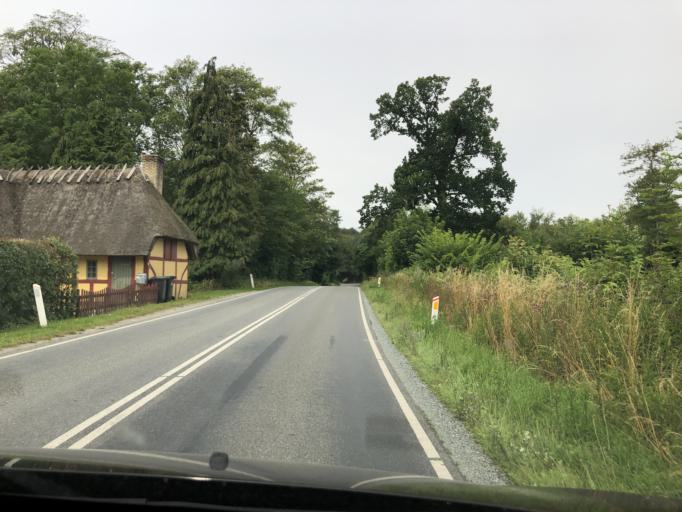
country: DK
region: South Denmark
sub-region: Assens Kommune
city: Glamsbjerg
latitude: 55.2884
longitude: 10.0896
